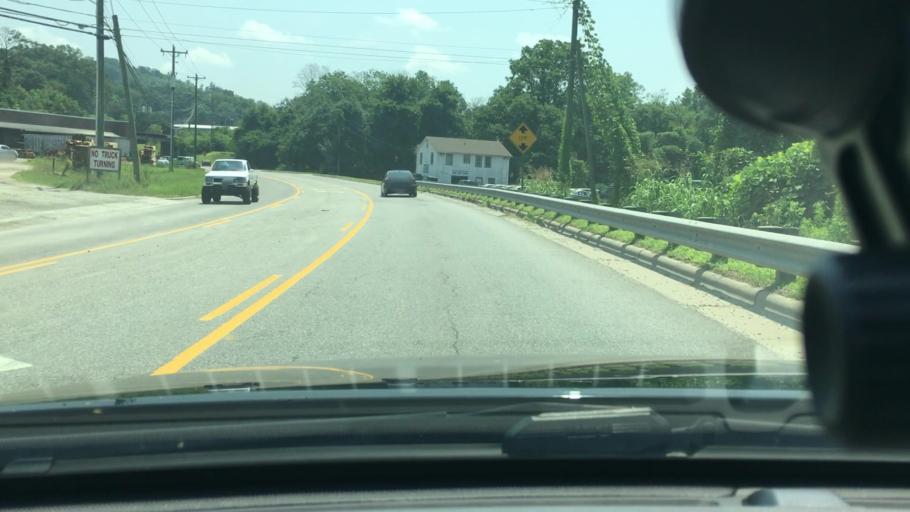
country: US
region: North Carolina
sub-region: McDowell County
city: Marion
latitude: 35.6608
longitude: -81.9713
